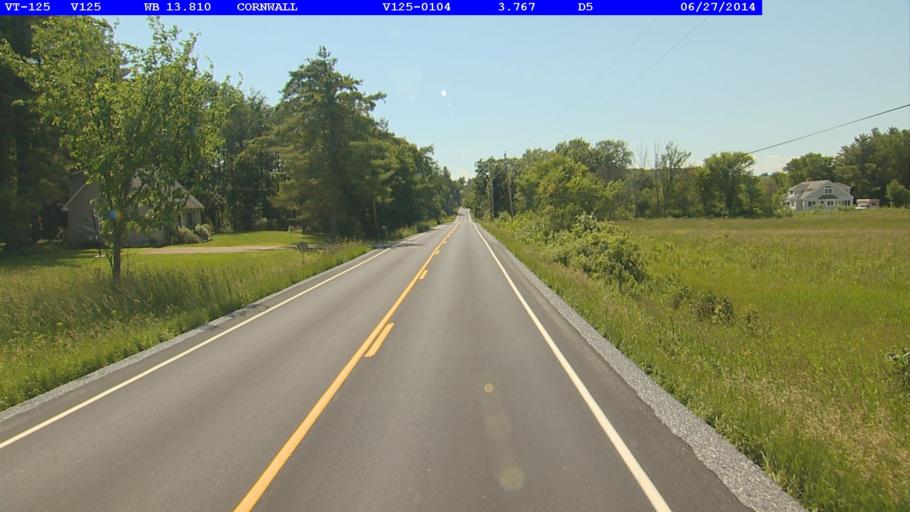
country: US
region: Vermont
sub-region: Addison County
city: Middlebury (village)
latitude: 44.0084
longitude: -73.1985
